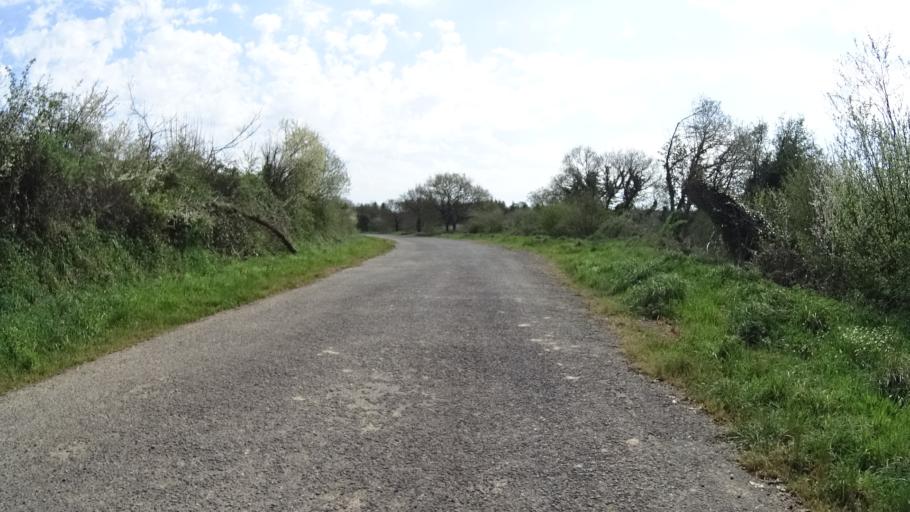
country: FR
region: Brittany
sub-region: Departement du Finistere
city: Sizun
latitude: 48.4270
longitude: -4.1026
